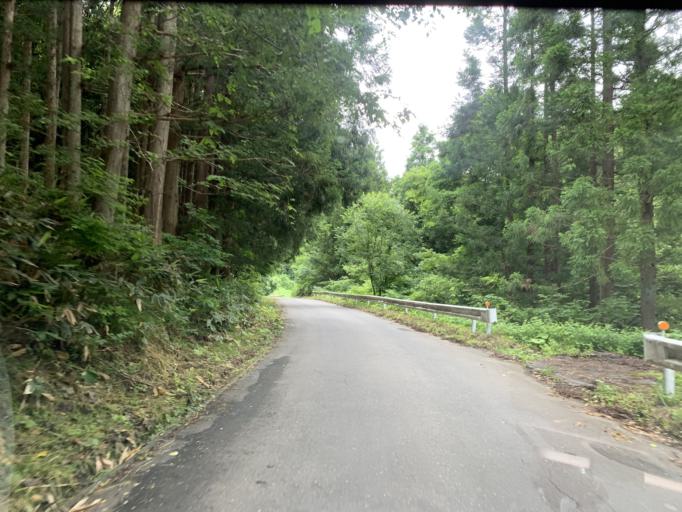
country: JP
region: Iwate
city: Ichinoseki
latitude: 38.9658
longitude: 140.9062
